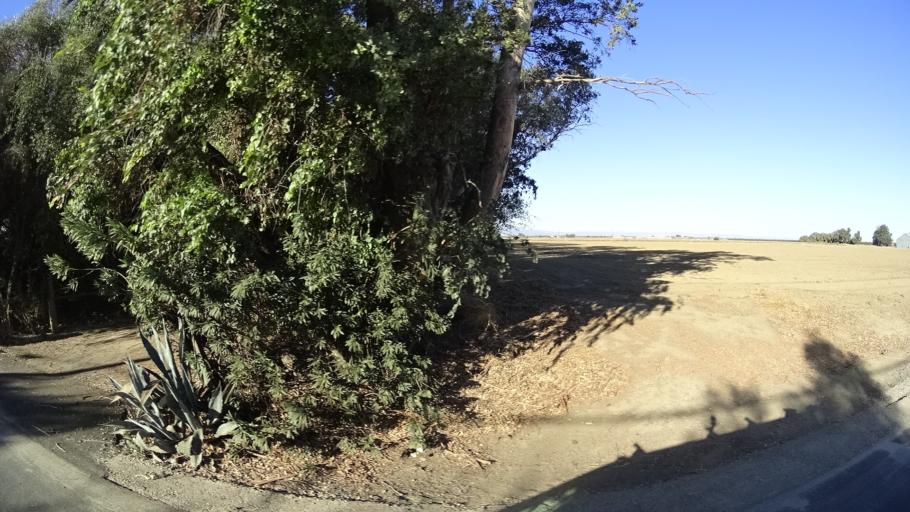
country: US
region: California
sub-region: Yolo County
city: Woodland
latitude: 38.6217
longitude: -121.7850
